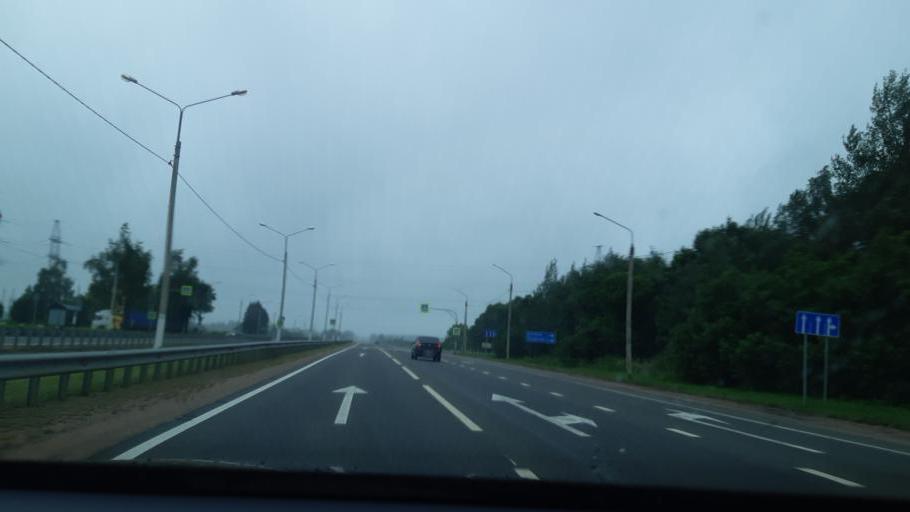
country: RU
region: Smolensk
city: Talashkino
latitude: 54.6581
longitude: 32.1612
